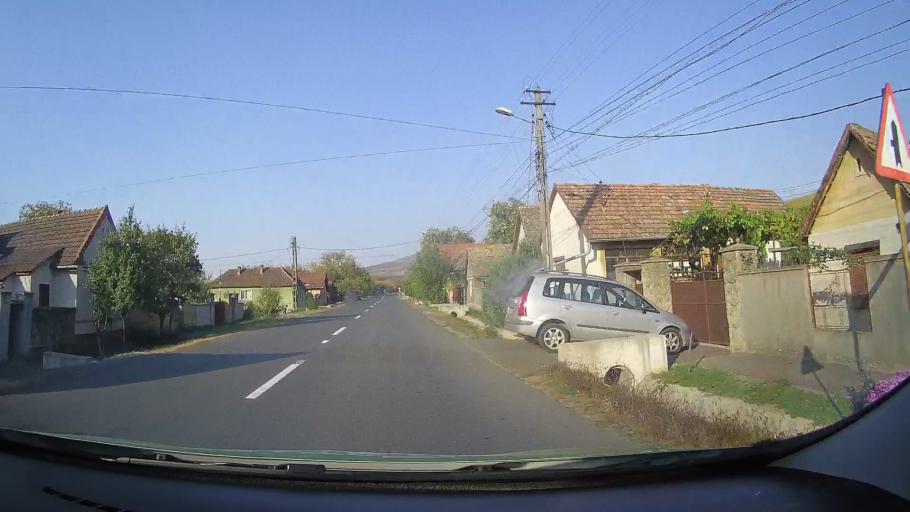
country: RO
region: Arad
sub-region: Comuna Paulis
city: Paulis
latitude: 46.1332
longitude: 21.6026
